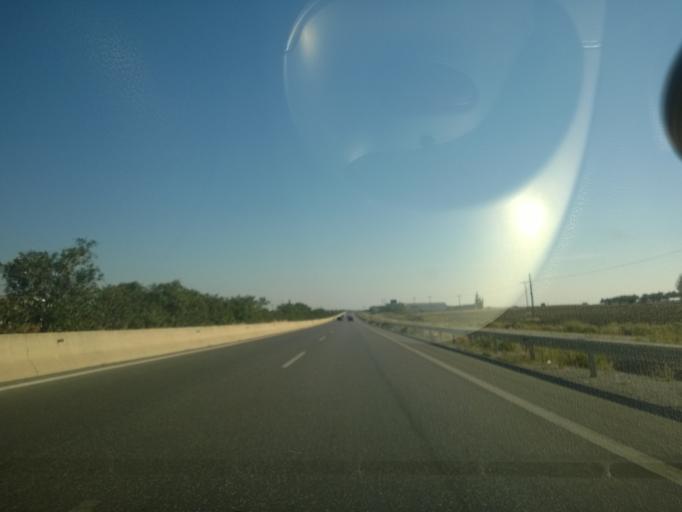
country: GR
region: Central Macedonia
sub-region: Nomos Chalkidikis
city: Lakkoma
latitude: 40.3828
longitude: 23.0392
